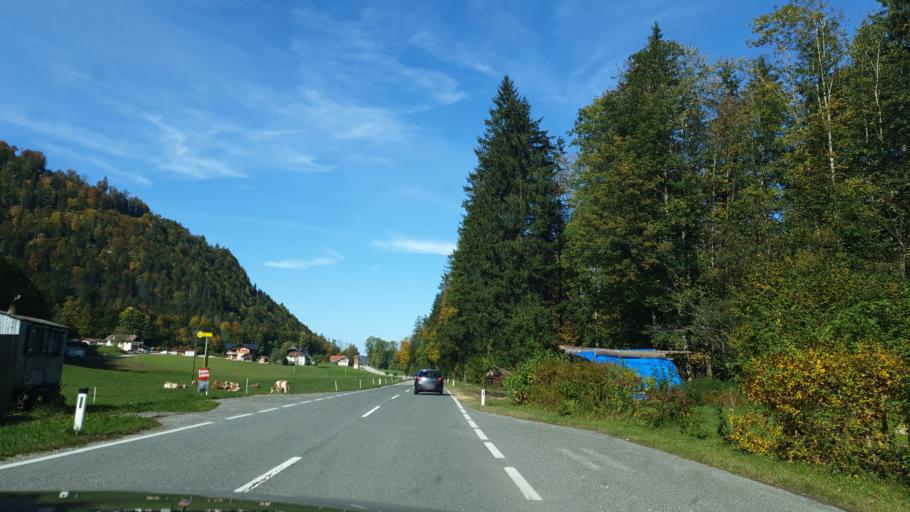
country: AT
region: Salzburg
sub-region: Politischer Bezirk Salzburg-Umgebung
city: Hintersee
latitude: 47.7219
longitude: 13.2792
